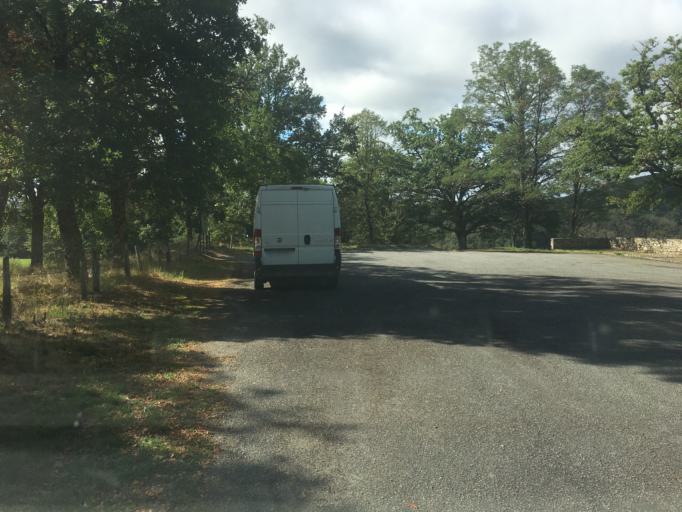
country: FR
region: Auvergne
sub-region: Departement du Cantal
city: Champagnac
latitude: 45.4133
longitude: 2.3915
